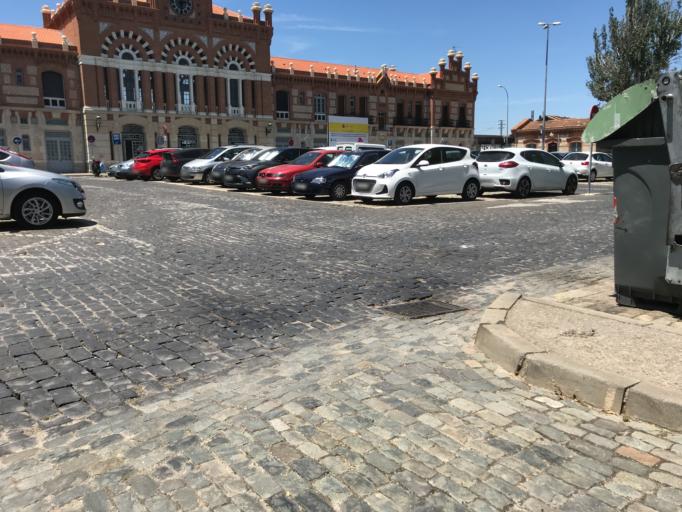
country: ES
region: Madrid
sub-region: Provincia de Madrid
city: Aranjuez
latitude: 40.0347
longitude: -3.6176
